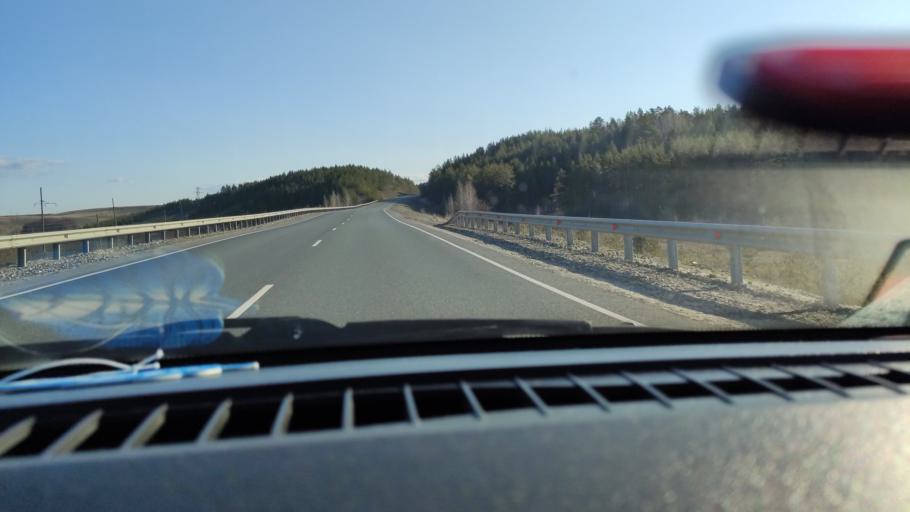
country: RU
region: Saratov
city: Khvalynsk
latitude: 52.5301
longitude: 48.0286
